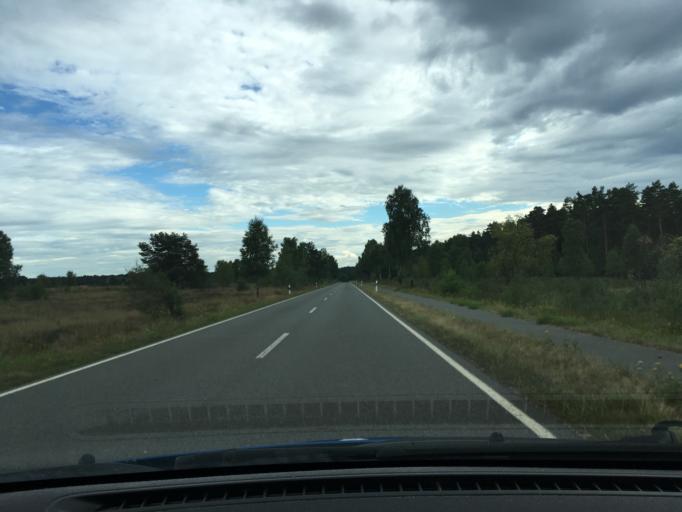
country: DE
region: Lower Saxony
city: Jesteburg
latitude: 53.2446
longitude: 9.9192
